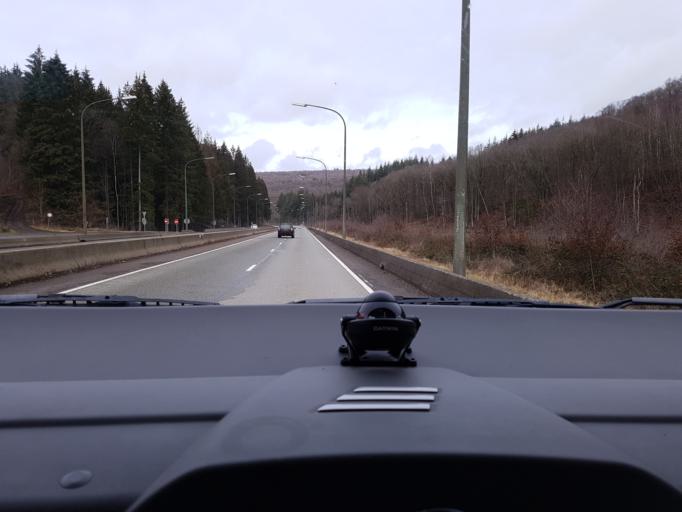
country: BE
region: Wallonia
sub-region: Province du Luxembourg
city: Tenneville
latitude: 50.1413
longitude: 5.4517
